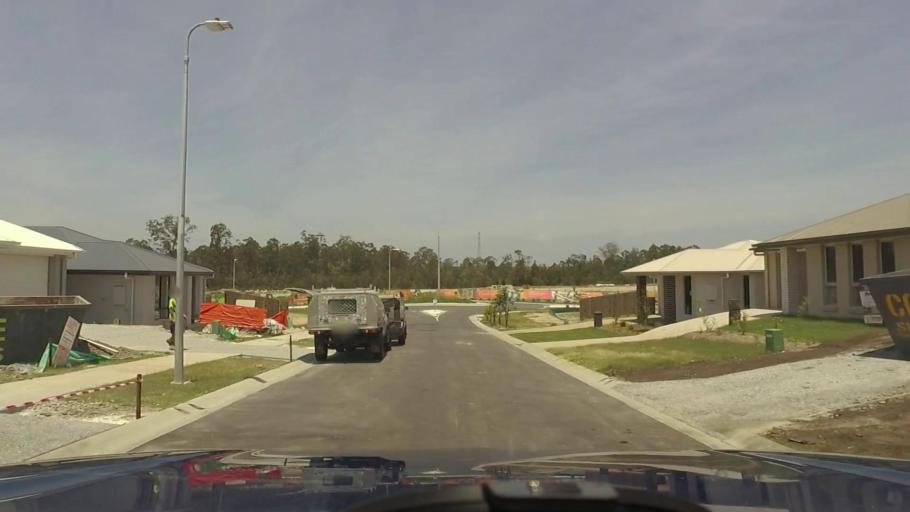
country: AU
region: Queensland
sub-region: Logan
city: Chambers Flat
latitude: -27.8089
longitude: 153.1241
